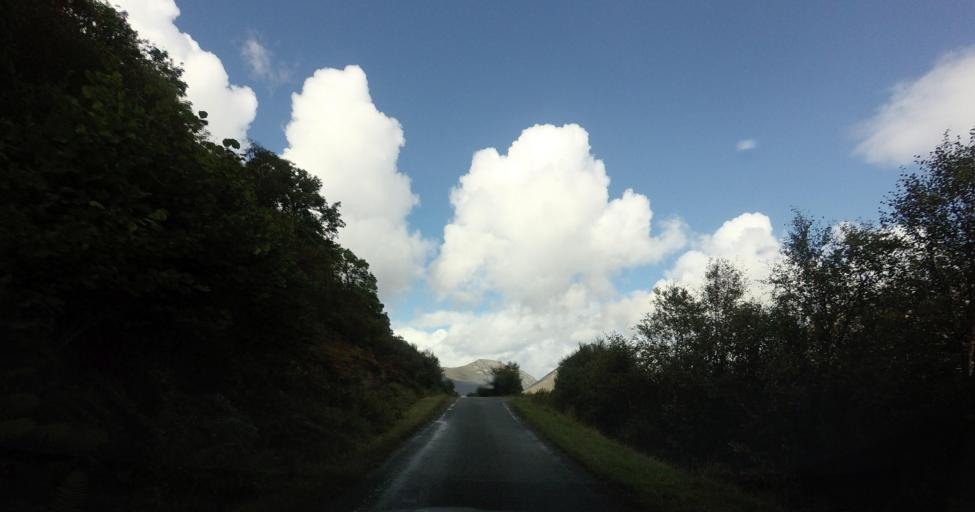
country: GB
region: Scotland
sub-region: Highland
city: Portree
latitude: 57.2036
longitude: -6.0273
